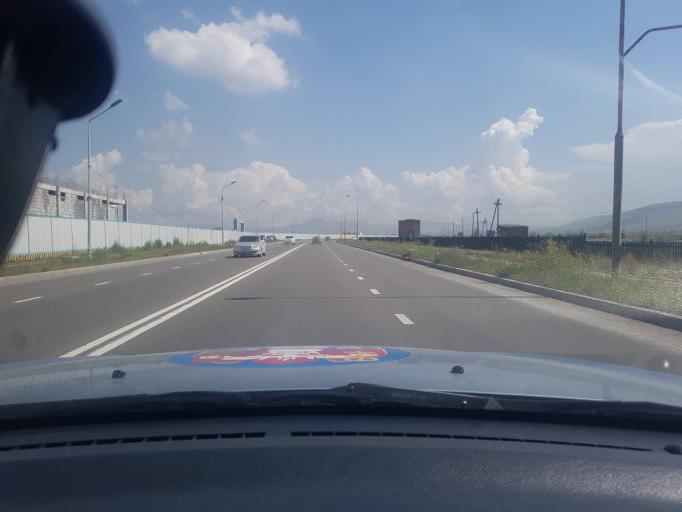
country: MN
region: Ulaanbaatar
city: Ulaanbaatar
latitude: 47.9051
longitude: 106.9688
